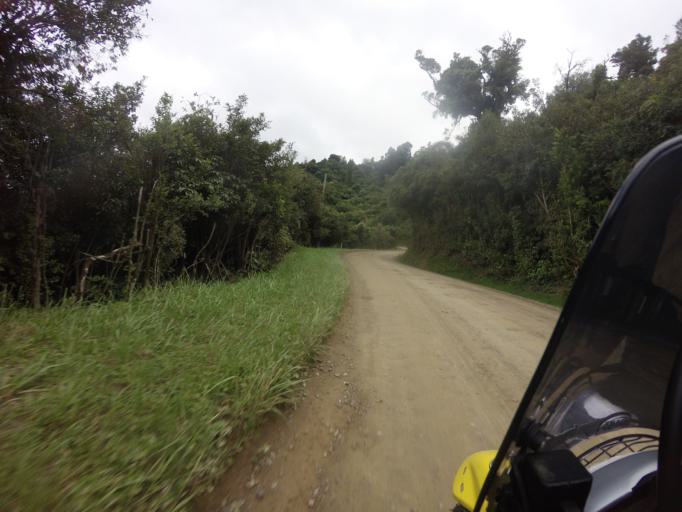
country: NZ
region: Hawke's Bay
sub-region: Wairoa District
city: Wairoa
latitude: -38.7701
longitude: 177.1352
